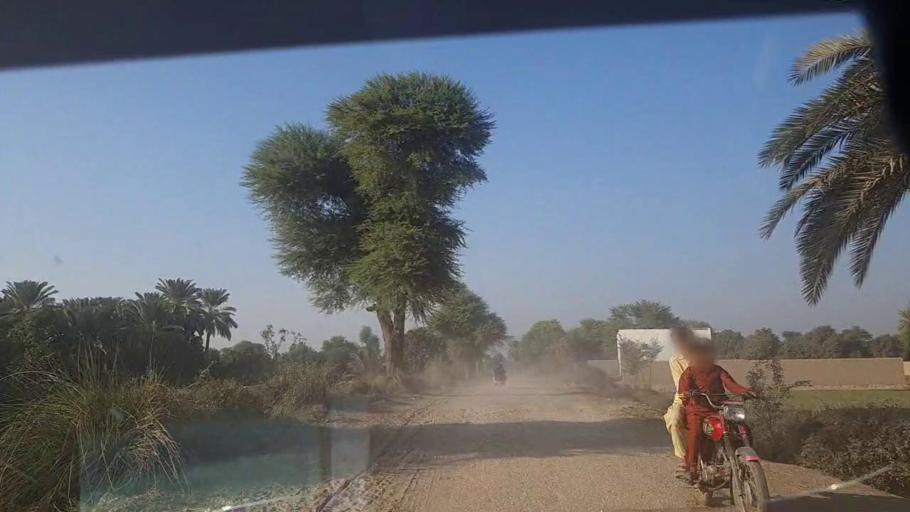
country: PK
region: Sindh
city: Sobhadero
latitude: 27.2678
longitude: 68.3481
